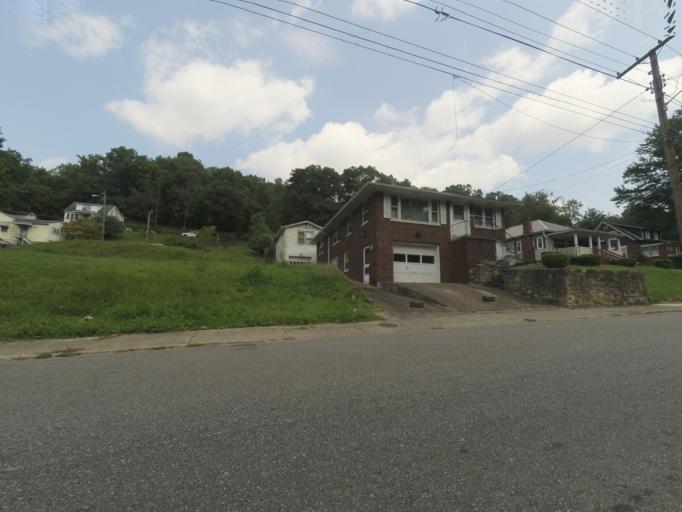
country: US
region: West Virginia
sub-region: Cabell County
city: Huntington
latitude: 38.4172
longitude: -82.4063
